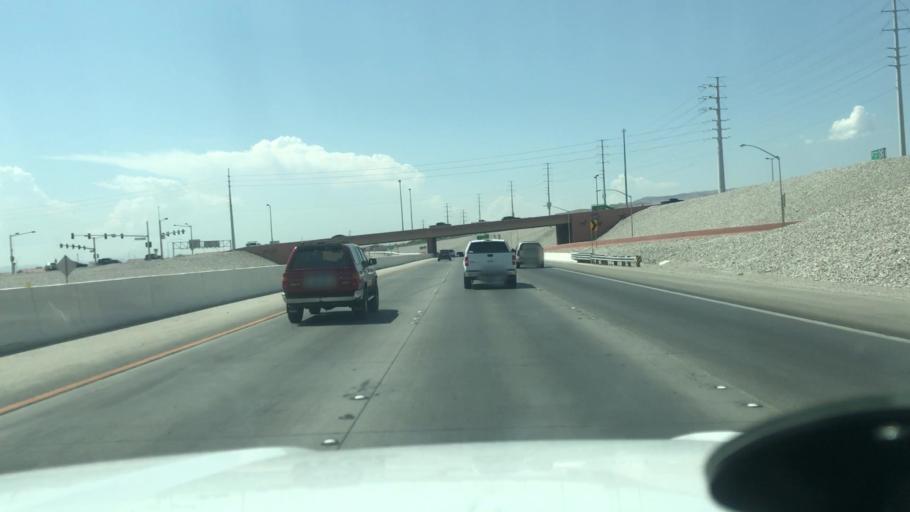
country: US
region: Nevada
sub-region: Clark County
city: Summerlin South
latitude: 36.1937
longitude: -115.3424
